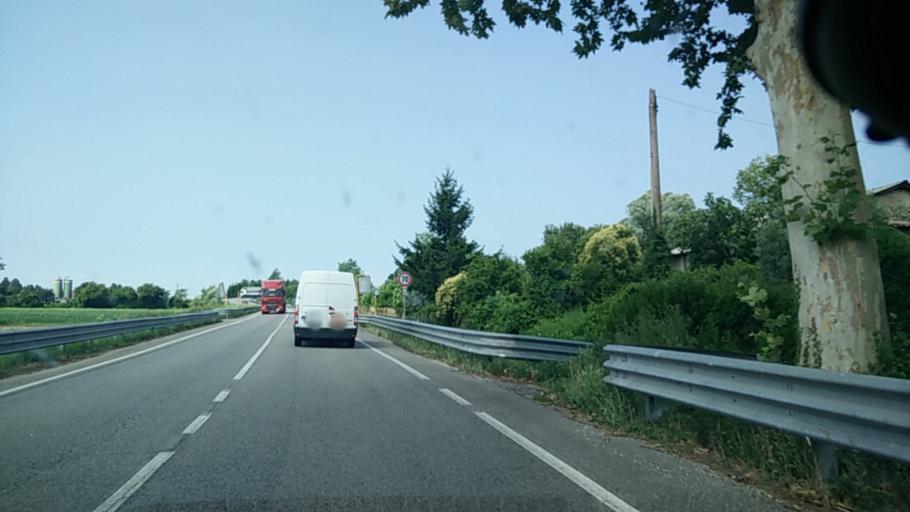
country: IT
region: Veneto
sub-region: Provincia di Treviso
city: Portobuffole
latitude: 45.8555
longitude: 12.5306
